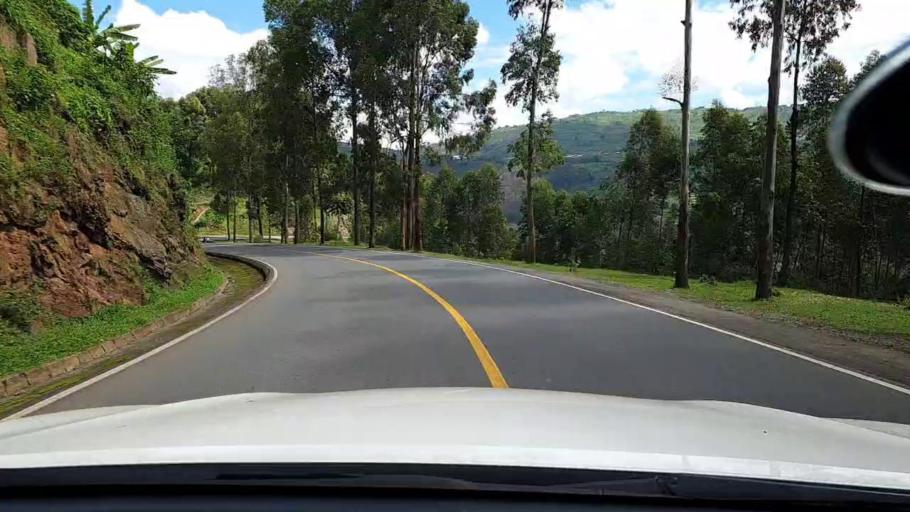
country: RW
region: Kigali
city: Kigali
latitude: -1.7757
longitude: 29.9267
